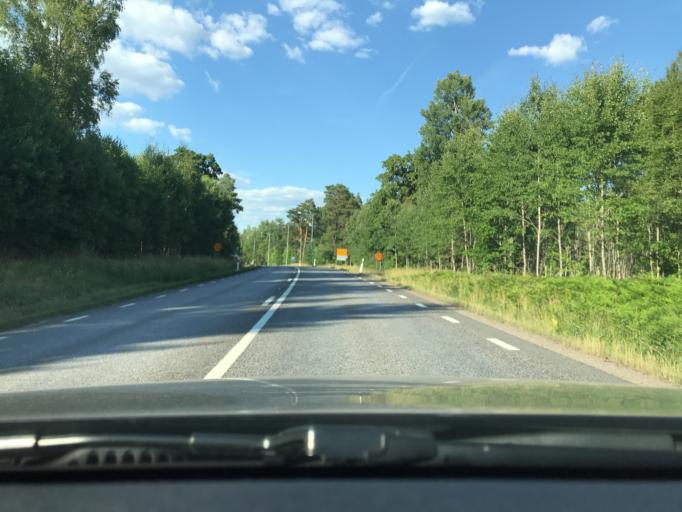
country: SE
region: Kronoberg
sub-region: Vaxjo Kommun
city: Vaexjoe
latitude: 56.8531
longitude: 14.7276
